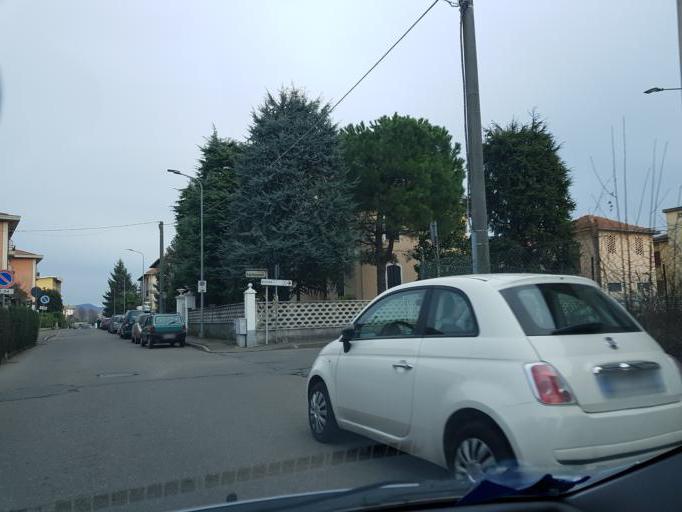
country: IT
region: Piedmont
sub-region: Provincia di Alessandria
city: Novi Ligure
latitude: 44.7640
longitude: 8.8009
